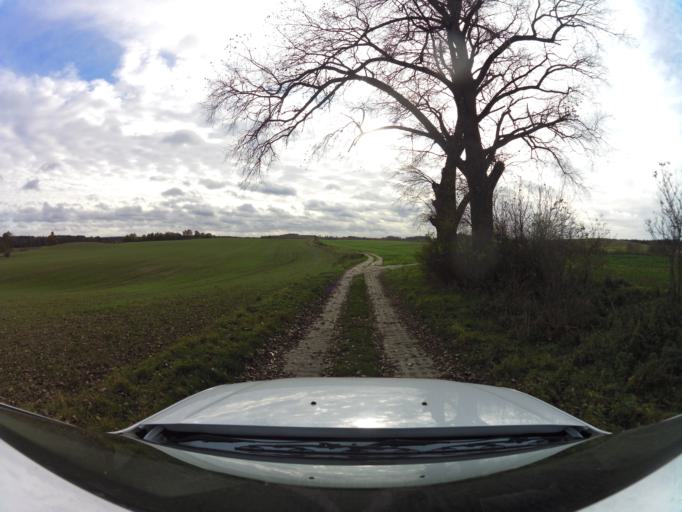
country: PL
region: West Pomeranian Voivodeship
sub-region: Powiat gryficki
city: Gryfice
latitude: 53.8824
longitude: 15.1138
